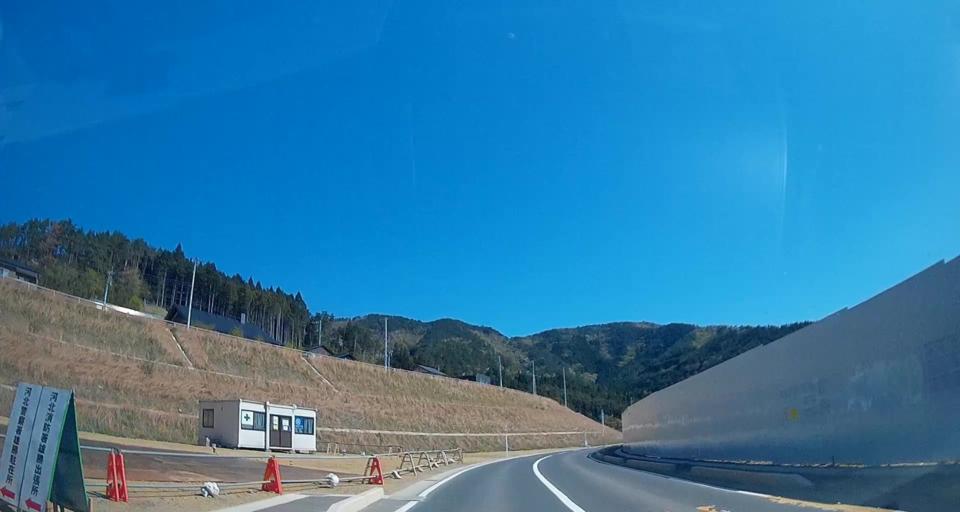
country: JP
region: Miyagi
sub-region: Oshika Gun
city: Onagawa Cho
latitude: 38.5198
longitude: 141.4678
